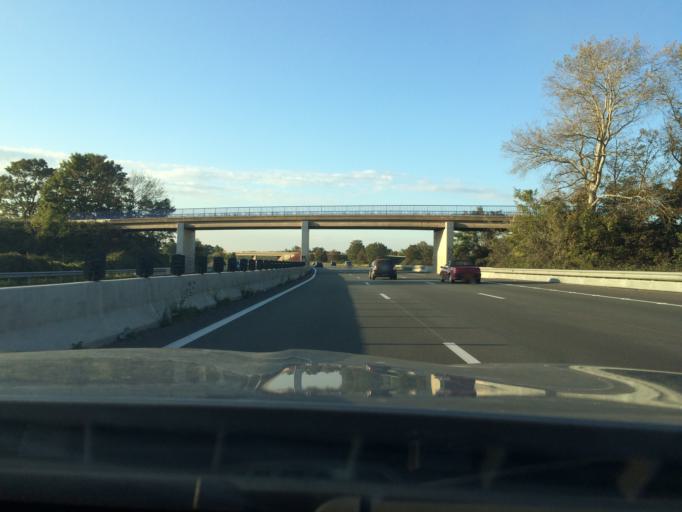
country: FR
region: Ile-de-France
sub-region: Departement de l'Essonne
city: Le Coudray-Montceaux
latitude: 48.5541
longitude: 2.4930
